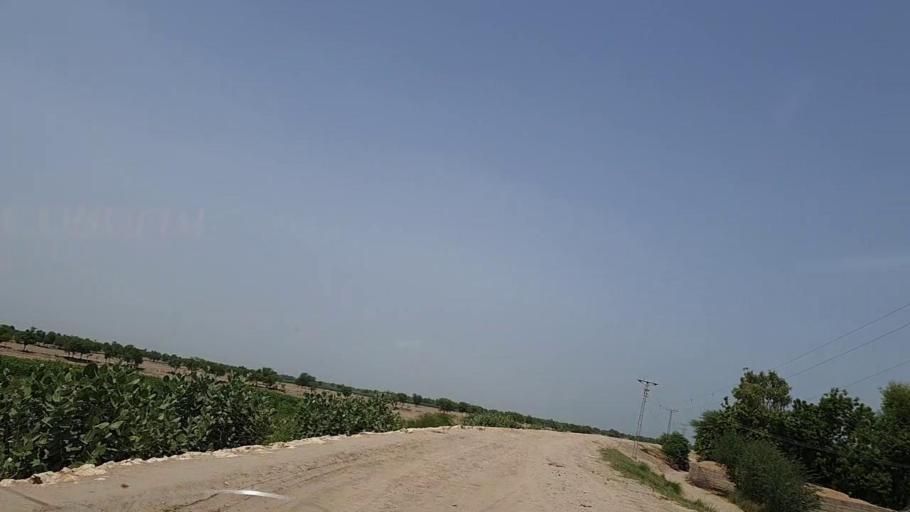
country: PK
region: Sindh
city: Tharu Shah
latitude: 27.0151
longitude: 68.1029
